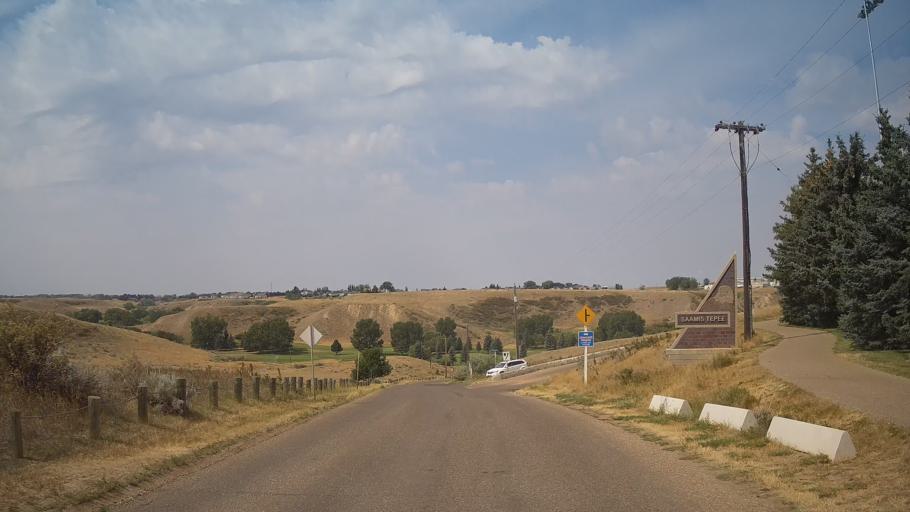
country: CA
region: Alberta
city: Medicine Hat
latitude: 50.0121
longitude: -110.6889
